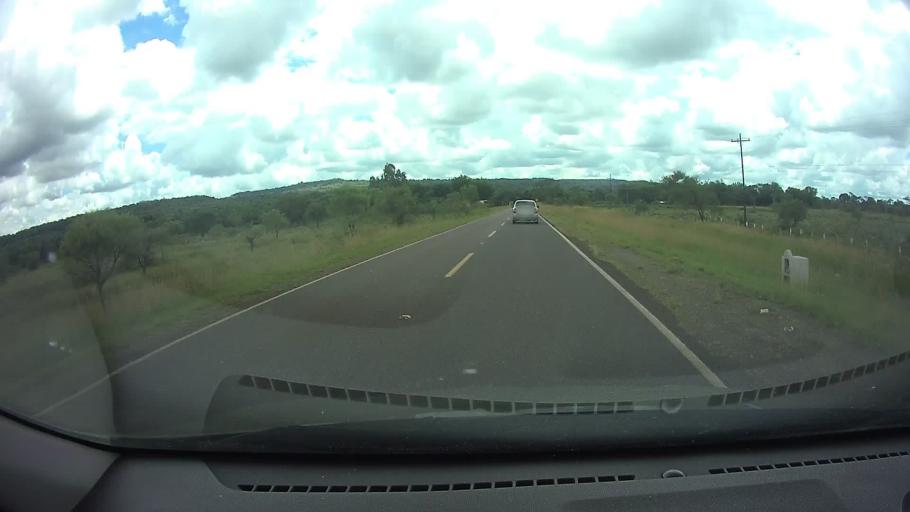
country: PY
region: Paraguari
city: Ybycui
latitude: -25.9008
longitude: -56.9733
